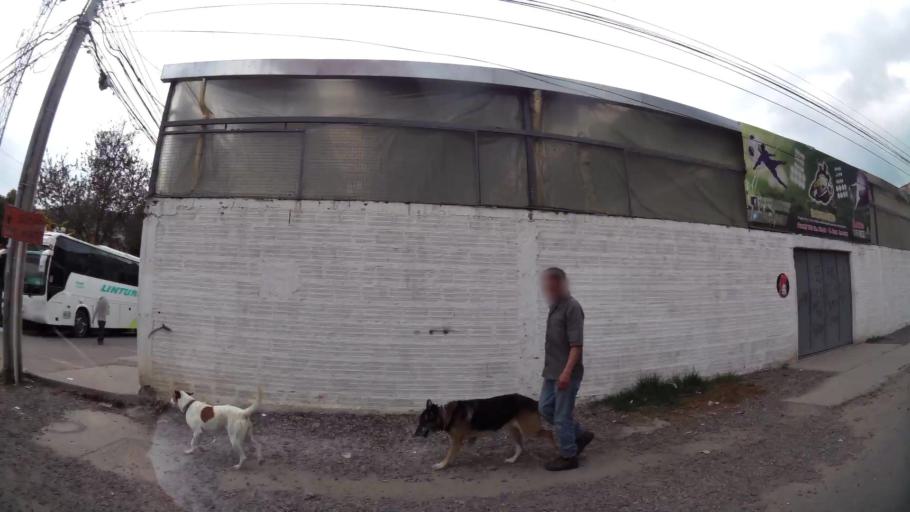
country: CO
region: Cundinamarca
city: La Calera
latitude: 4.7586
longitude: -74.0312
